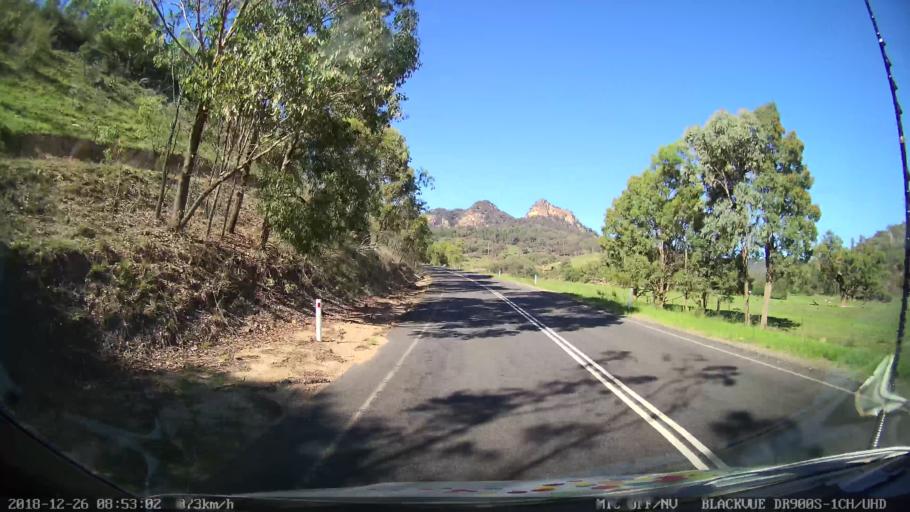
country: AU
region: New South Wales
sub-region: Mid-Western Regional
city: Kandos
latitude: -32.6002
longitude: 150.0803
